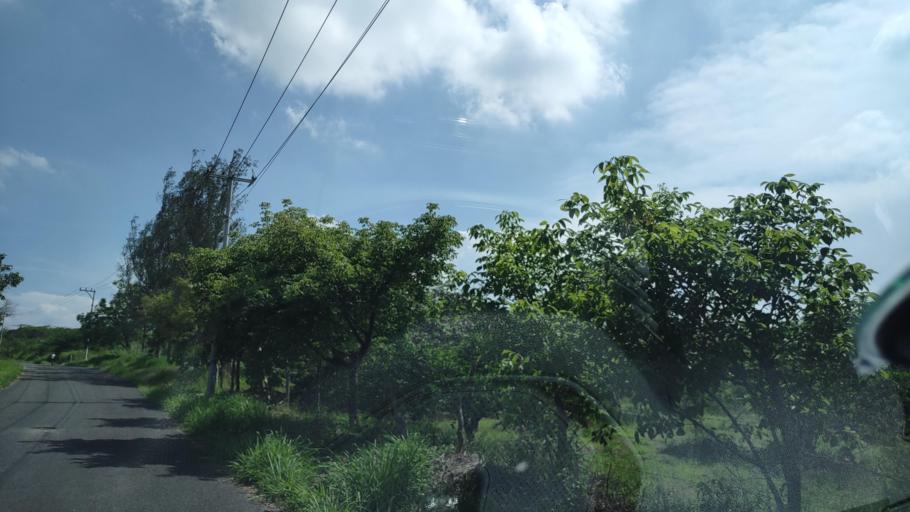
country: MX
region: Veracruz
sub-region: Emiliano Zapata
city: Dos Rios
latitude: 19.4337
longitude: -96.8097
